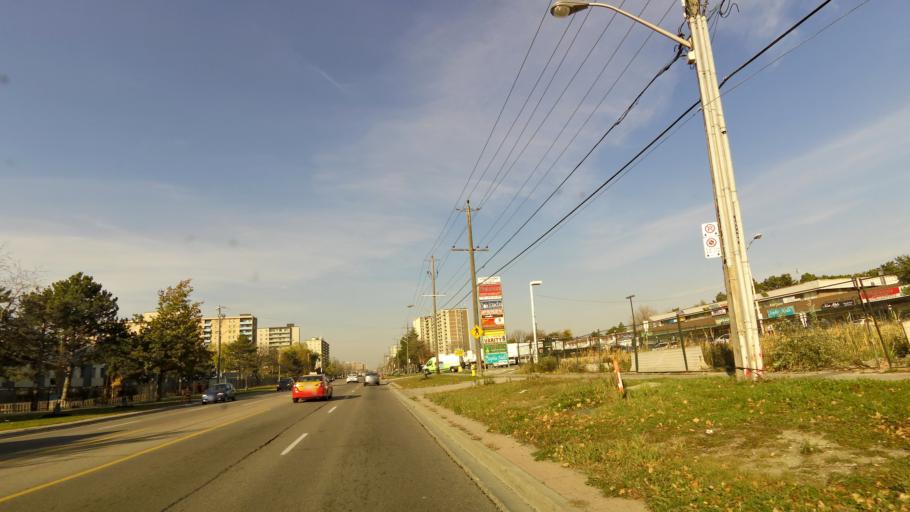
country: CA
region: Ontario
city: Concord
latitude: 43.7511
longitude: -79.5160
